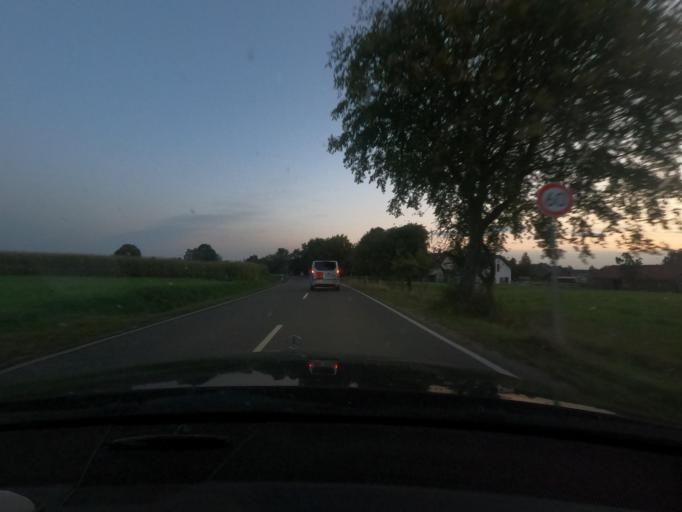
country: DE
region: North Rhine-Westphalia
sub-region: Regierungsbezirk Detmold
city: Salzkotten
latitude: 51.6501
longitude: 8.5941
